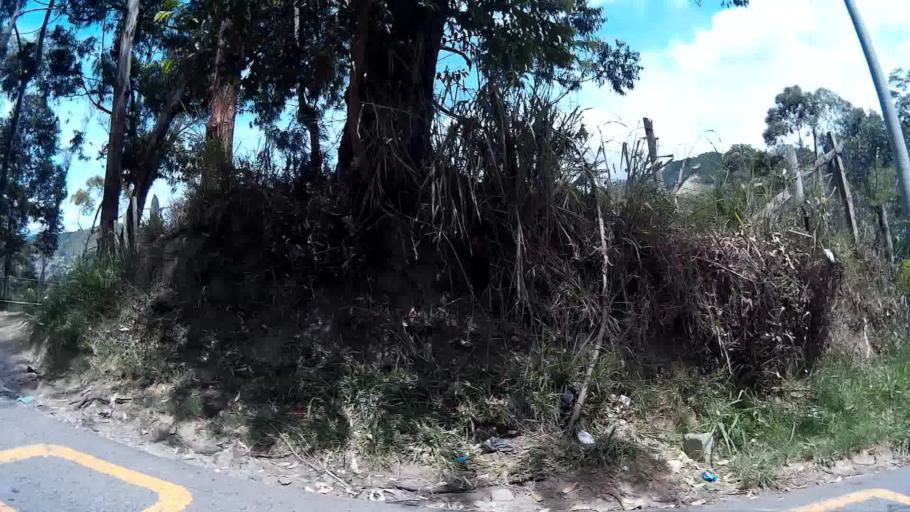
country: CO
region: Antioquia
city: Medellin
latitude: 6.2636
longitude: -75.6278
